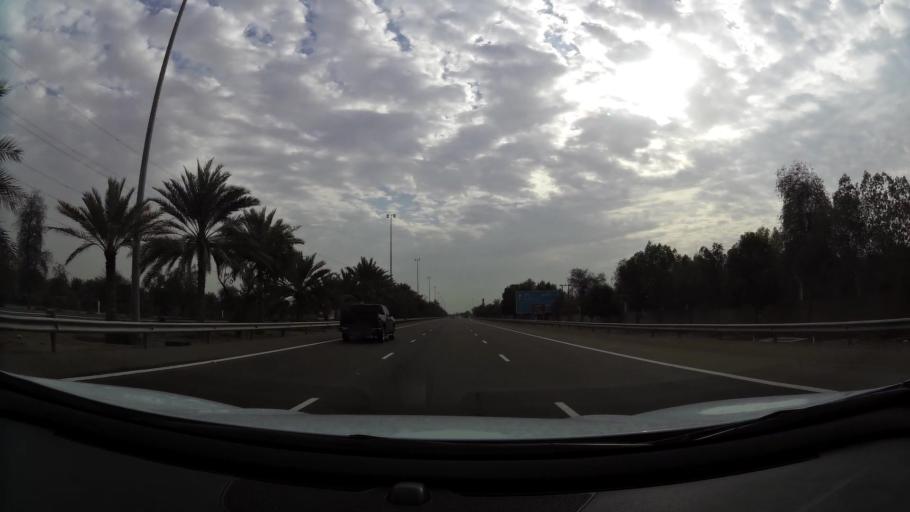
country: AE
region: Abu Dhabi
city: Al Ain
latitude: 24.2039
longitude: 55.4119
